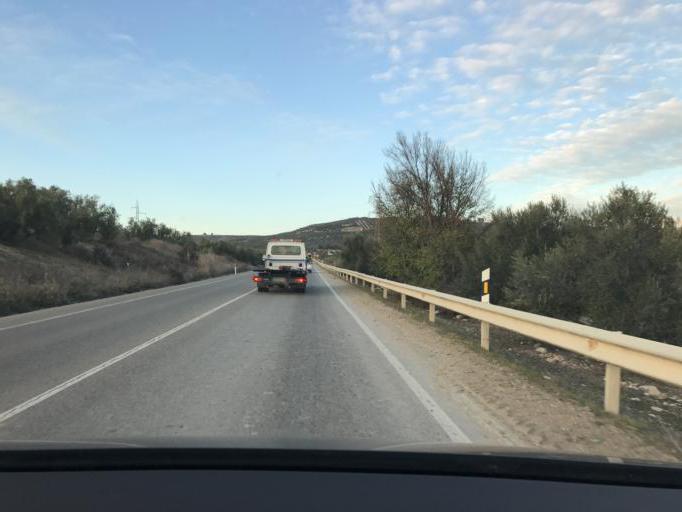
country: ES
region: Andalusia
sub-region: Provincia de Jaen
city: Ubeda
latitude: 37.9881
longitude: -3.3822
